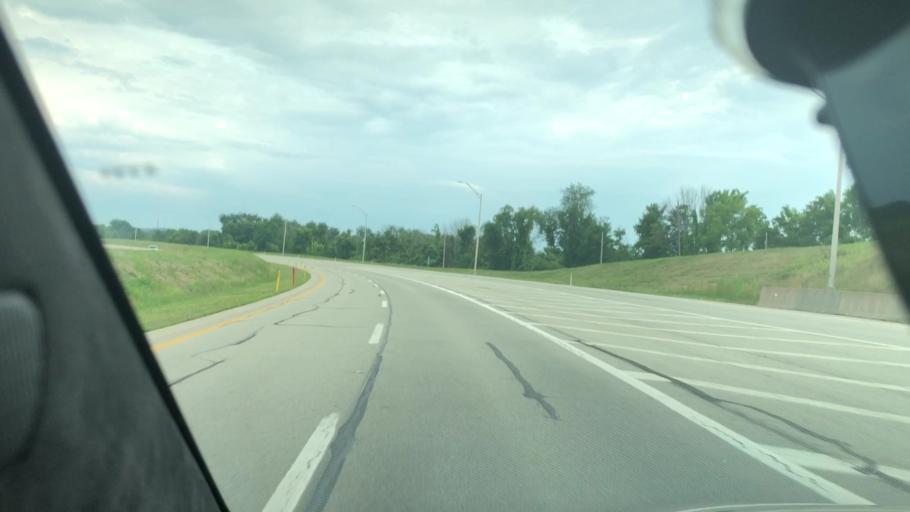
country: US
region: Pennsylvania
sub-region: Washington County
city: Baidland
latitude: 40.1893
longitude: -79.9896
